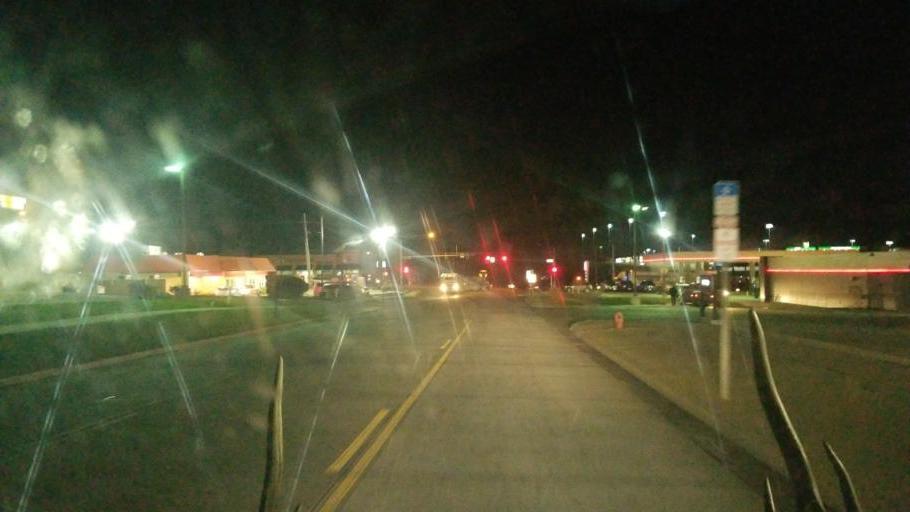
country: US
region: Missouri
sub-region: Jackson County
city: Oak Grove
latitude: 39.0129
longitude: -94.1272
